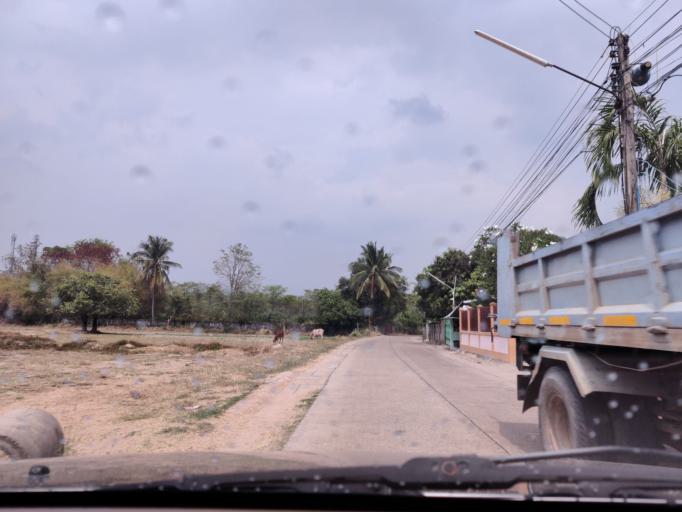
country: TH
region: Sisaket
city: Si Sa Ket
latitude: 15.1055
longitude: 104.3547
